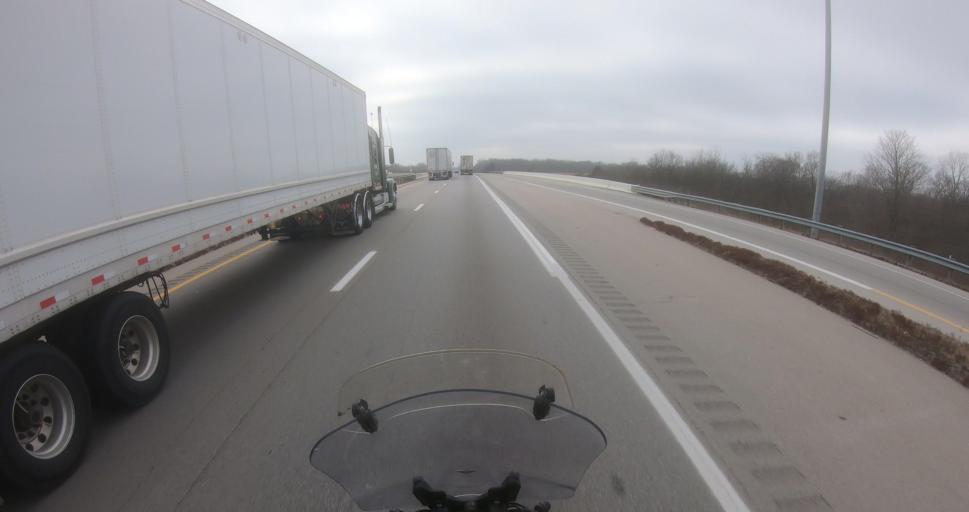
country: US
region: Ohio
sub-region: Miami County
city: Piqua
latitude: 40.0993
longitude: -84.2291
